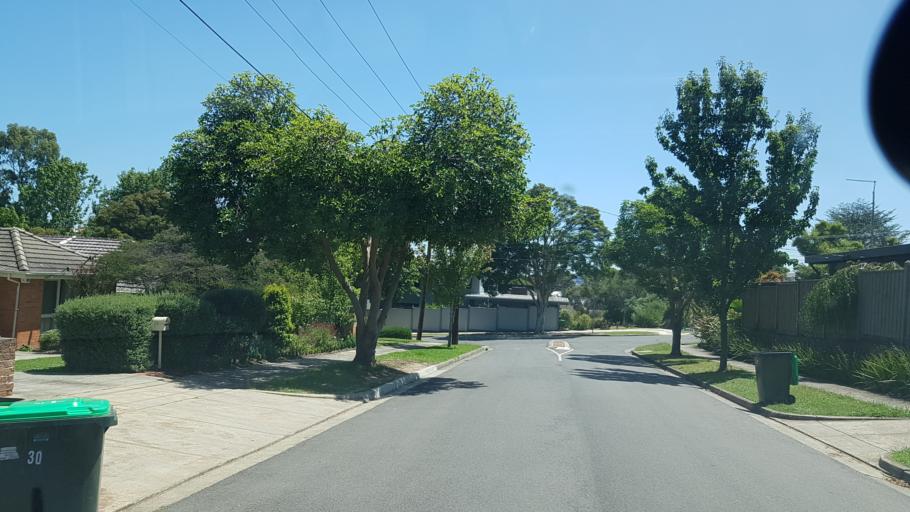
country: AU
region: Victoria
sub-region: Manningham
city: Bulleen
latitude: -37.7616
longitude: 145.0996
